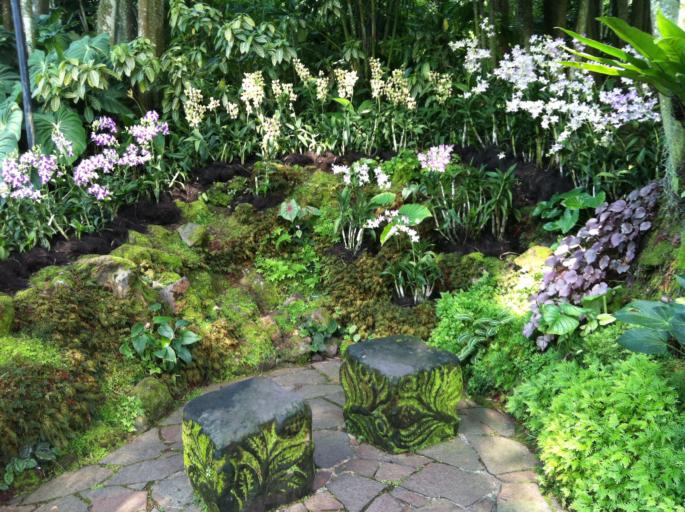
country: SG
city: Singapore
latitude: 1.3120
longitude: 103.8145
